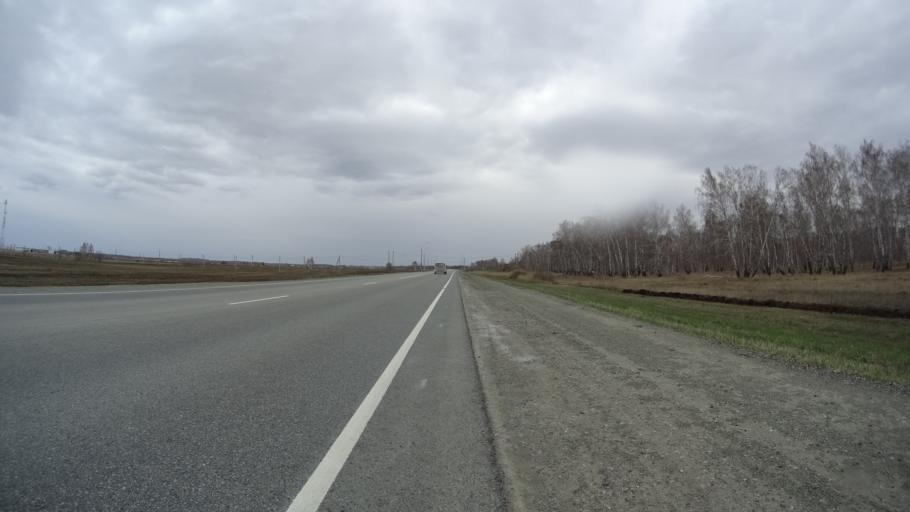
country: RU
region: Chelyabinsk
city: Krasnogorskiy
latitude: 54.6873
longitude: 61.2480
